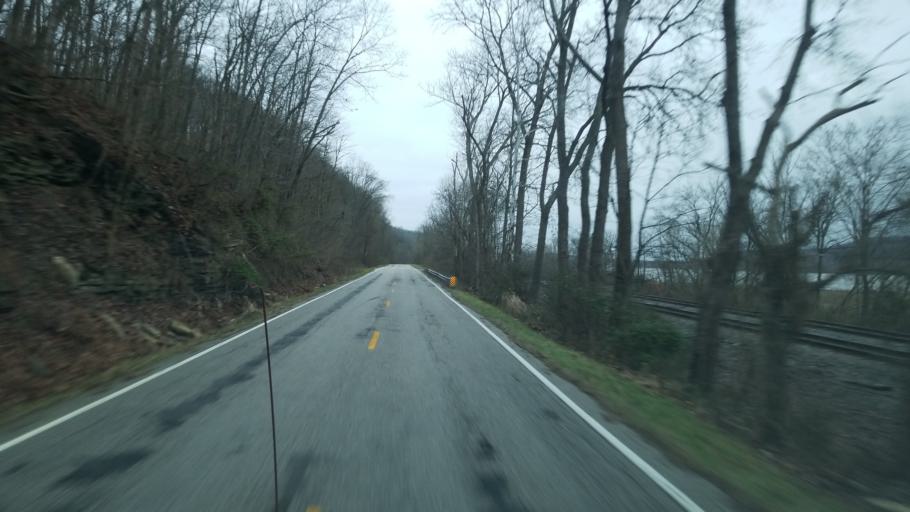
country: US
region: Kentucky
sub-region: Bracken County
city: Augusta
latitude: 38.7670
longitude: -84.0346
